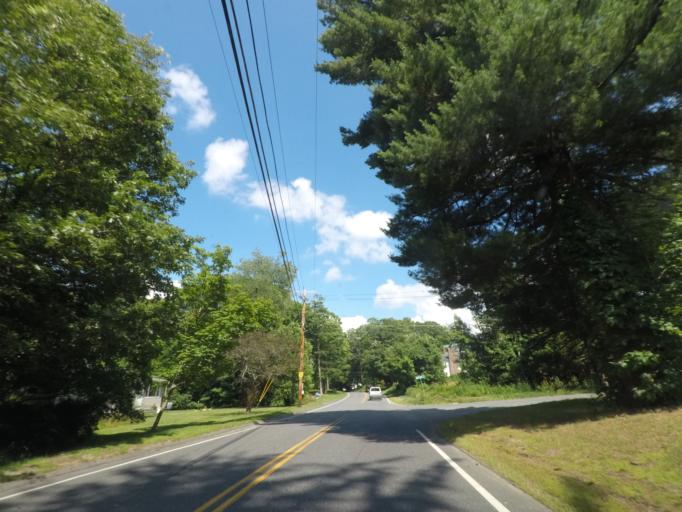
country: US
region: Massachusetts
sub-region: Hampden County
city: Monson Center
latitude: 42.1142
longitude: -72.2812
